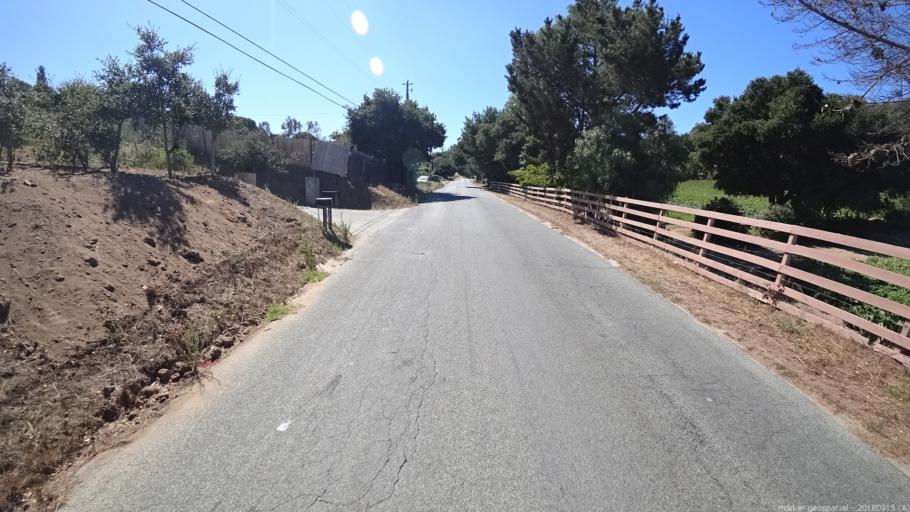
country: US
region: California
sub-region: Monterey County
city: Las Lomas
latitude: 36.8512
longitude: -121.7085
